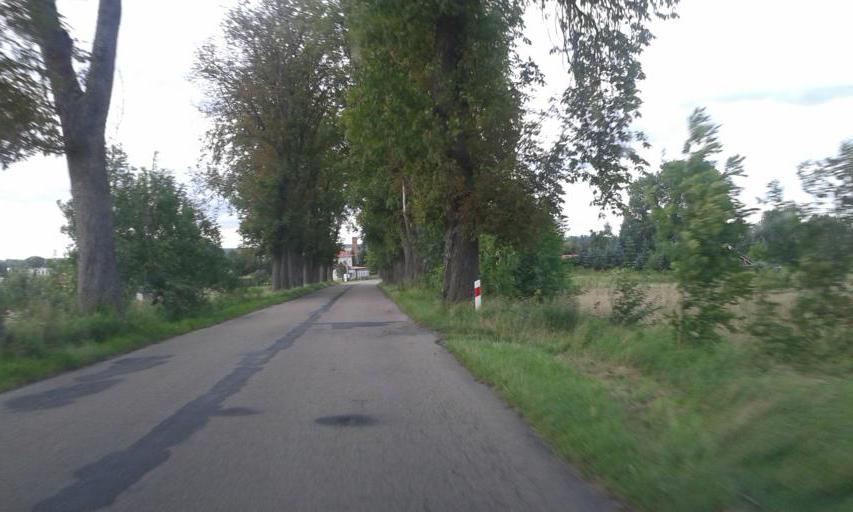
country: PL
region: West Pomeranian Voivodeship
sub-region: Powiat szczecinecki
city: Barwice
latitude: 53.7335
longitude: 16.3553
